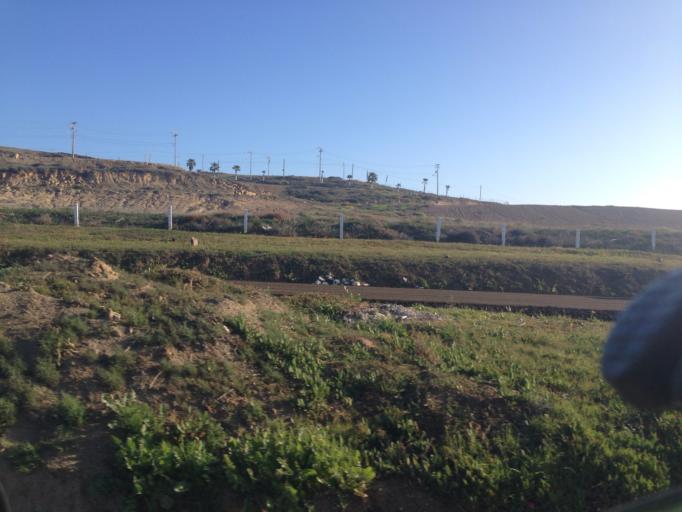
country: MX
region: Baja California
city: Primo Tapia
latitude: 32.2363
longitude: -116.9262
